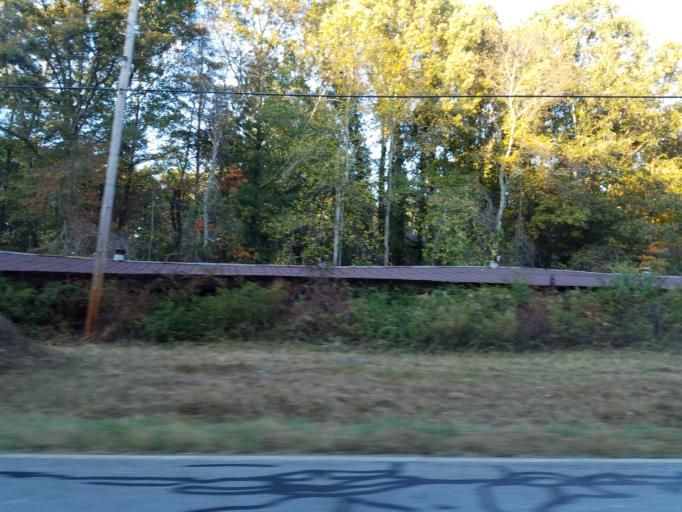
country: US
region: Georgia
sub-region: Lumpkin County
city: Dahlonega
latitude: 34.5481
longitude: -84.0910
